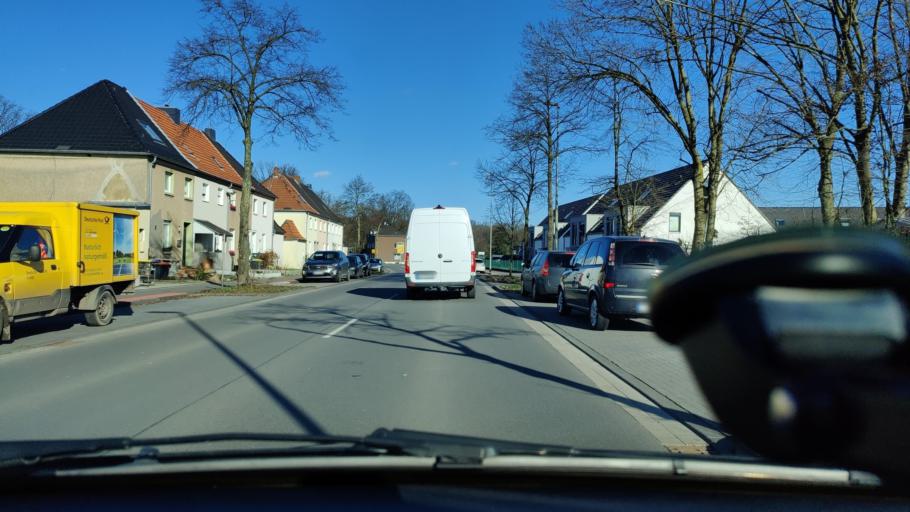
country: DE
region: North Rhine-Westphalia
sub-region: Regierungsbezirk Dusseldorf
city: Dinslaken
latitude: 51.5819
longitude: 6.7752
